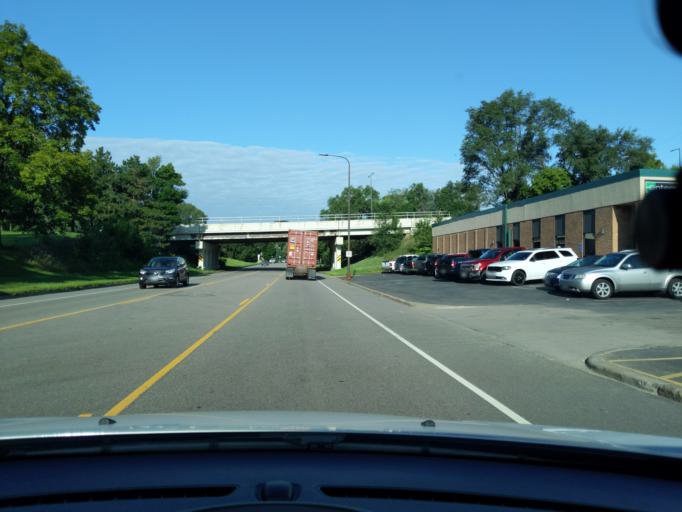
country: US
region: Minnesota
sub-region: Ramsey County
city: Falcon Heights
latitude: 44.9665
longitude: -93.1455
